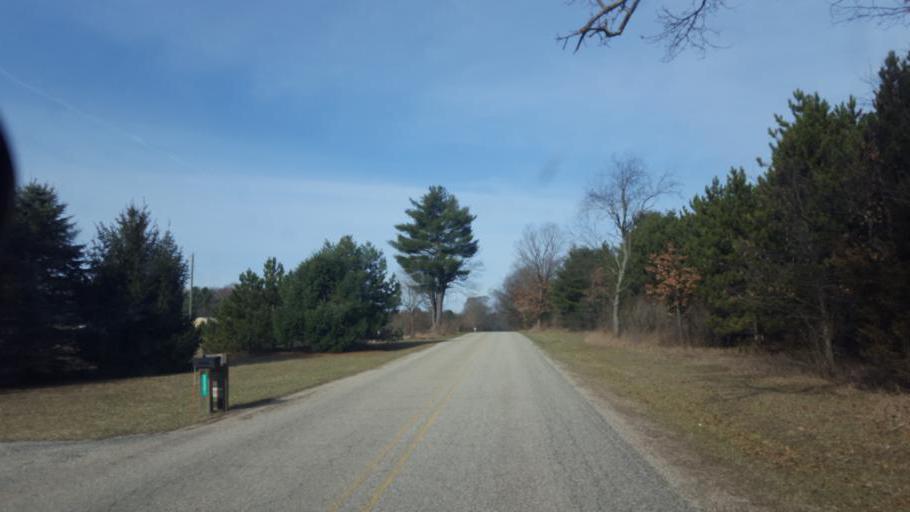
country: US
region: Michigan
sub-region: Montcalm County
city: Howard City
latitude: 43.5259
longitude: -85.5493
